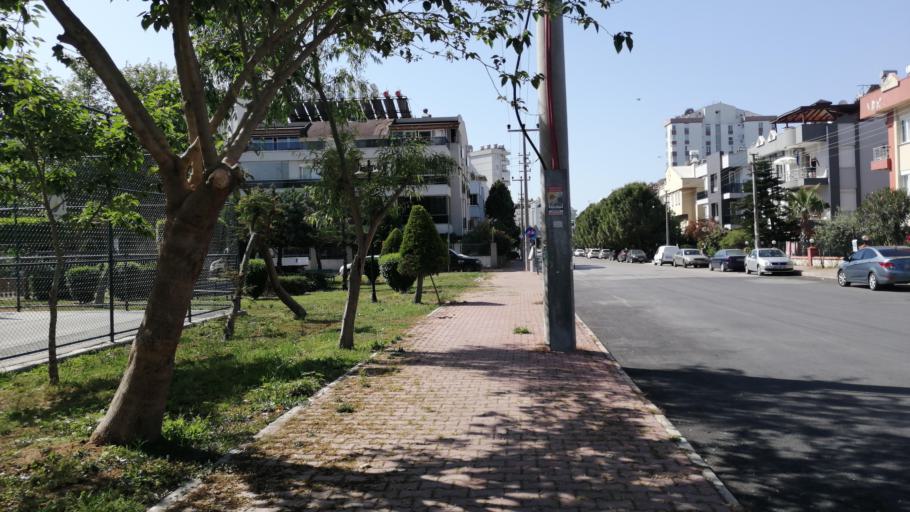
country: TR
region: Antalya
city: Antalya
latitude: 36.8591
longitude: 30.7831
